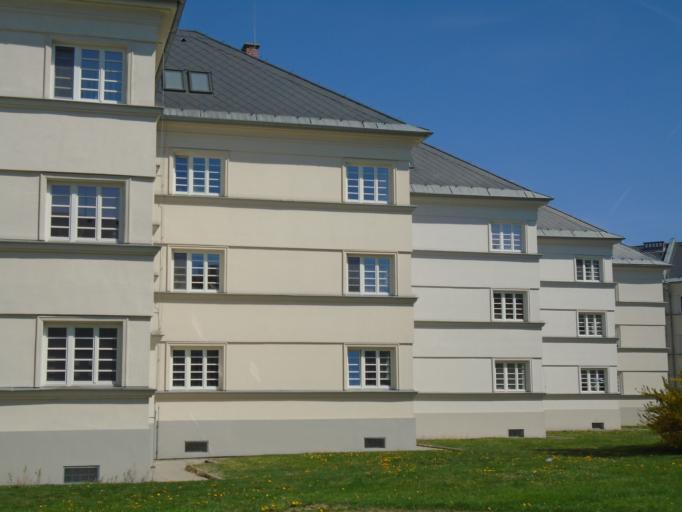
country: CZ
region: Moravskoslezsky
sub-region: Okres Ostrava-Mesto
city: Ostrava
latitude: 49.7935
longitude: 18.2600
